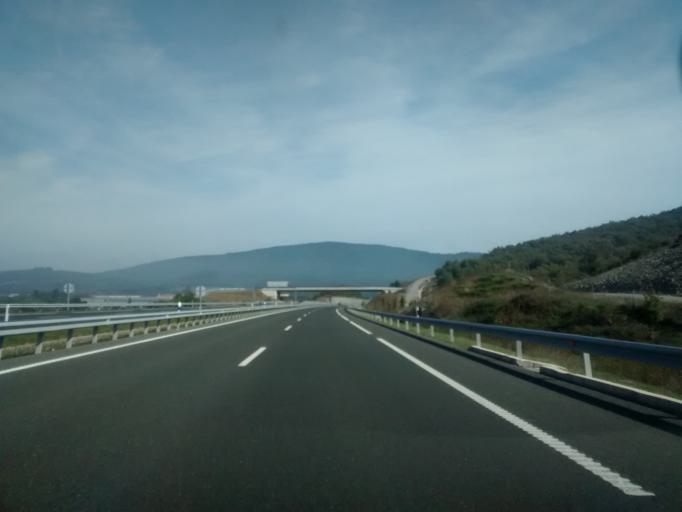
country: ES
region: Basque Country
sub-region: Provincia de Guipuzcoa
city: Leintz-Gatzaga
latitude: 42.9487
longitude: -2.6282
